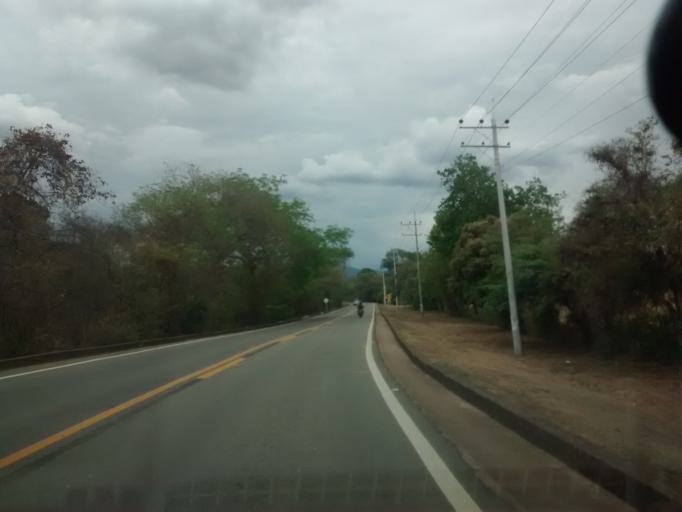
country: CO
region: Cundinamarca
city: Tocaima
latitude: 4.4409
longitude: -74.6760
